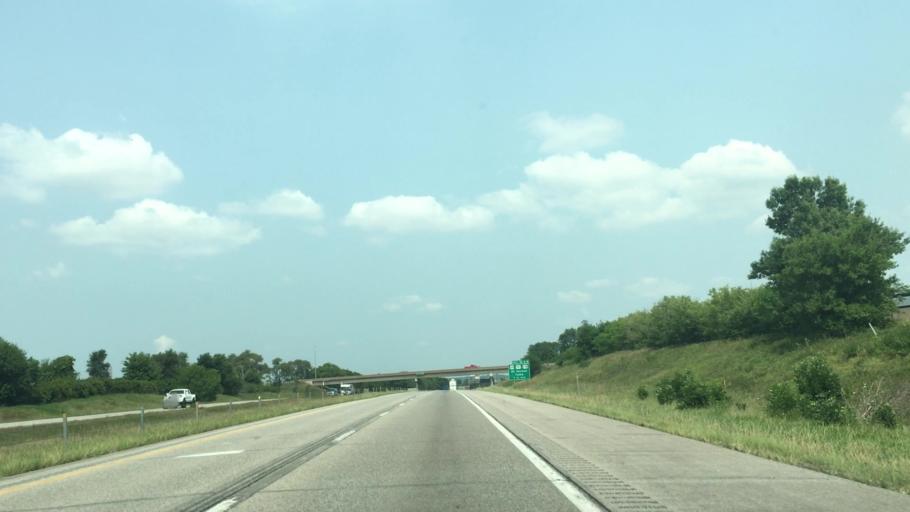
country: US
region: Iowa
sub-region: Linn County
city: Ely
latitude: 41.9023
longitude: -91.6717
